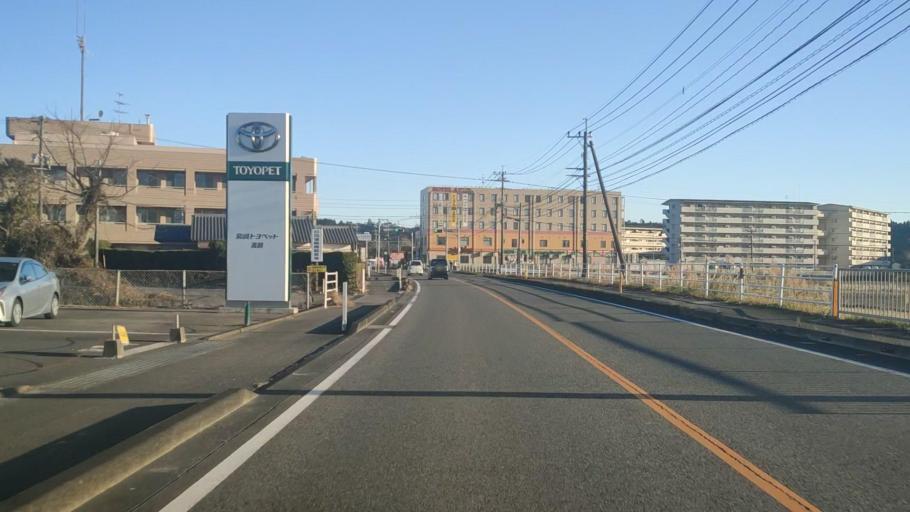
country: JP
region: Miyazaki
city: Takanabe
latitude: 32.1351
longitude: 131.5264
